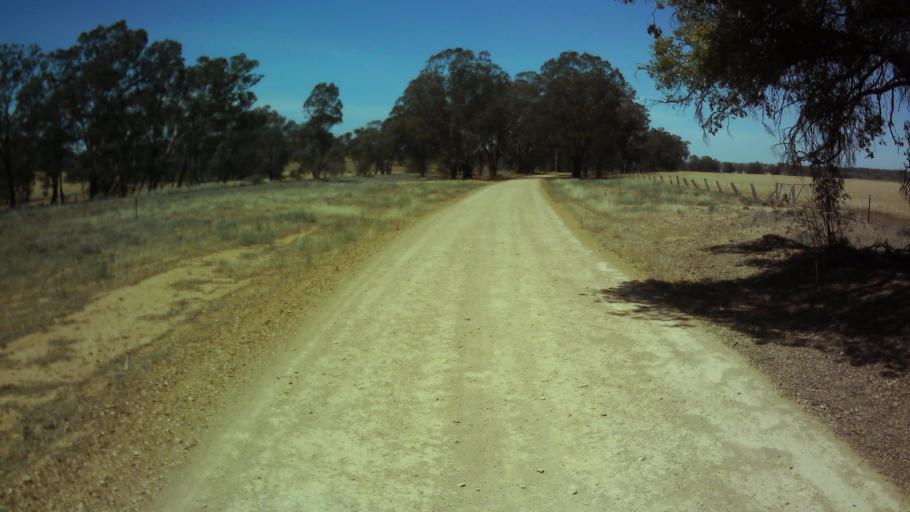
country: AU
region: New South Wales
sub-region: Weddin
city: Grenfell
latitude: -33.9211
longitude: 148.1964
